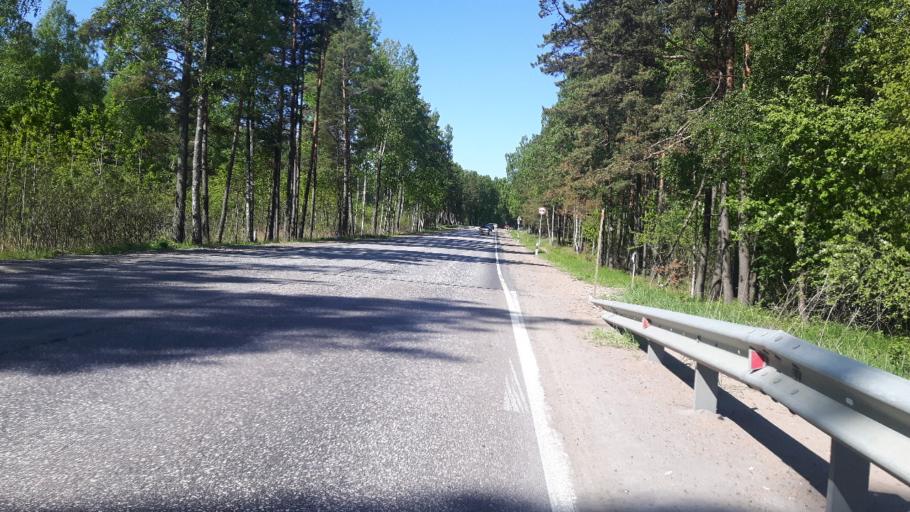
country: RU
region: Leningrad
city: Lebyazh'ye
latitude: 59.9566
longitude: 29.4751
